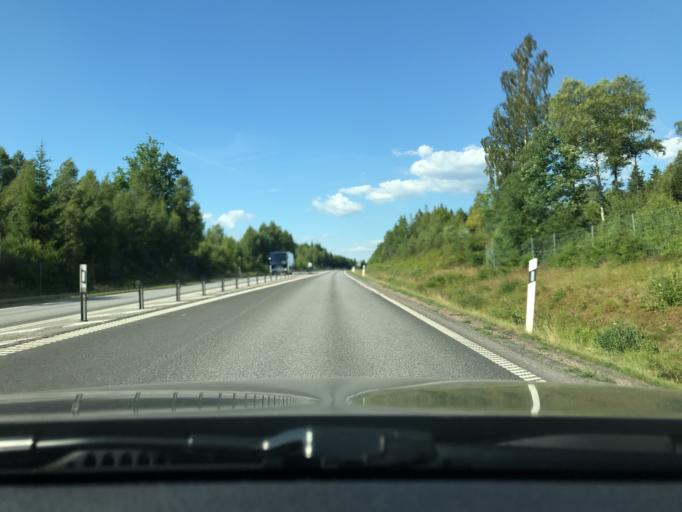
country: SE
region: Skane
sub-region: Osby Kommun
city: Osby
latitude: 56.4311
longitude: 14.0598
